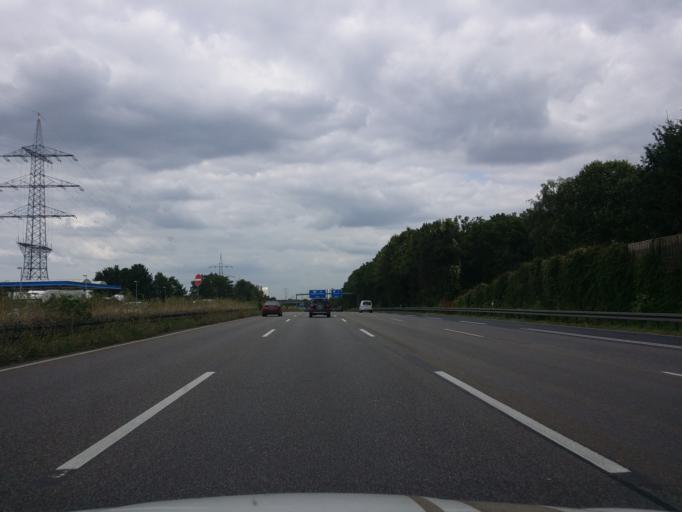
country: DE
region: Hesse
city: Sulzbach
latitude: 50.1189
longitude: 8.5431
